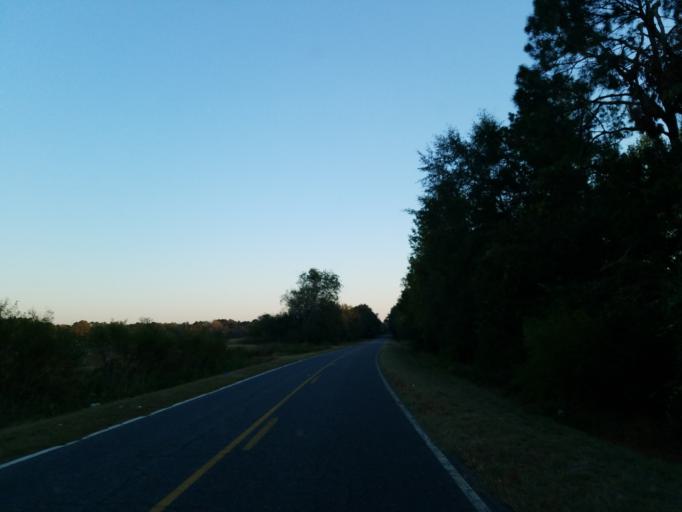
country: US
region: Georgia
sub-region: Ben Hill County
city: Fitzgerald
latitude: 31.6671
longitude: -83.3949
